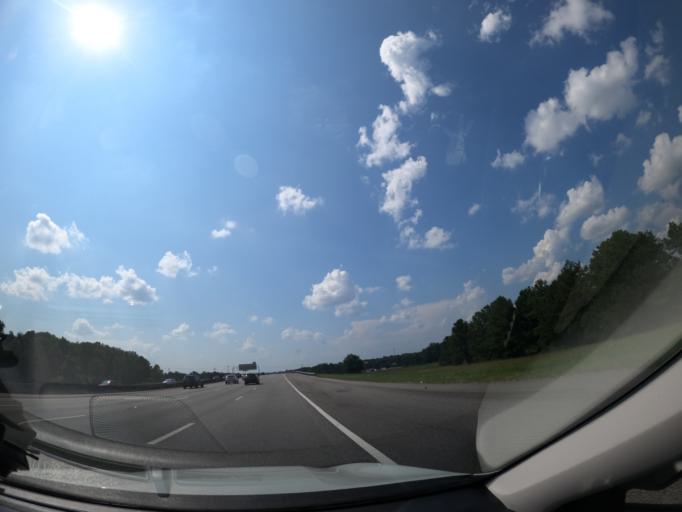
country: US
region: South Carolina
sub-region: Lexington County
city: Cayce
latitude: 33.9309
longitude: -81.0739
